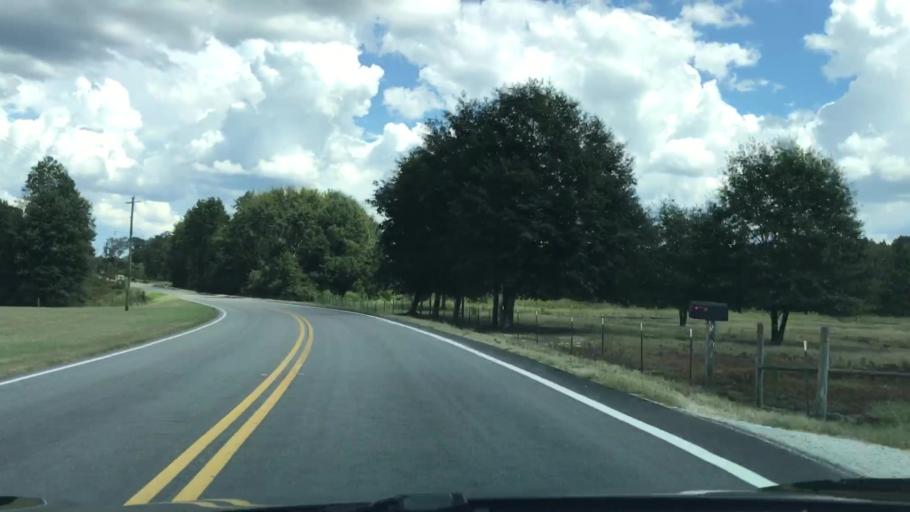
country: US
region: Georgia
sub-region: Greene County
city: Greensboro
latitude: 33.5588
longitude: -83.1318
